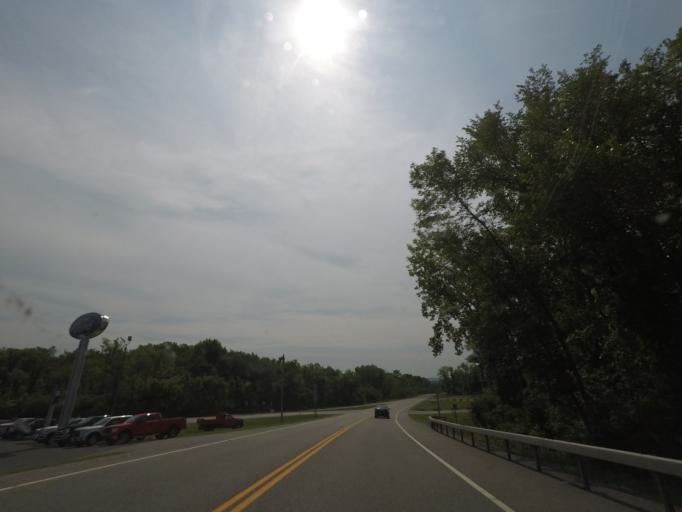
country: US
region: New York
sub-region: Saratoga County
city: Mechanicville
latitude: 42.8832
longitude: -73.6864
